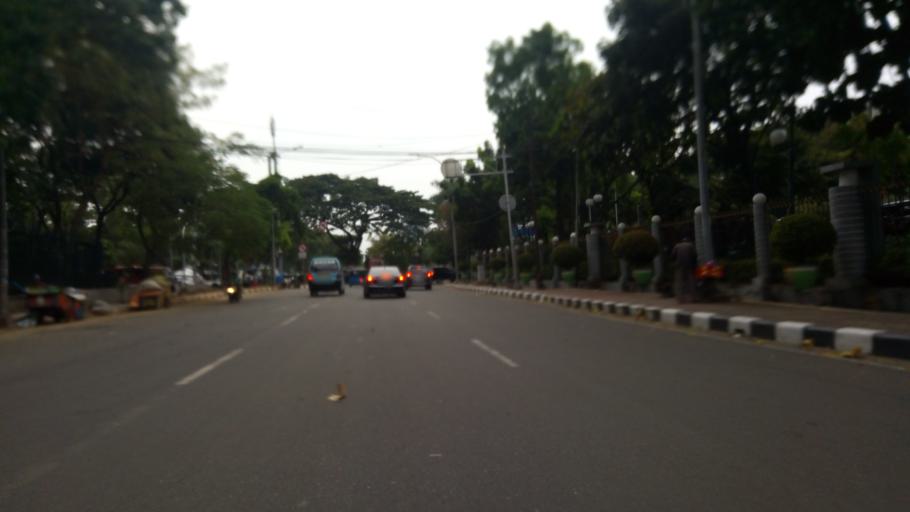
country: ID
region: Jakarta Raya
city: Jakarta
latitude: -6.1720
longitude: 106.8373
